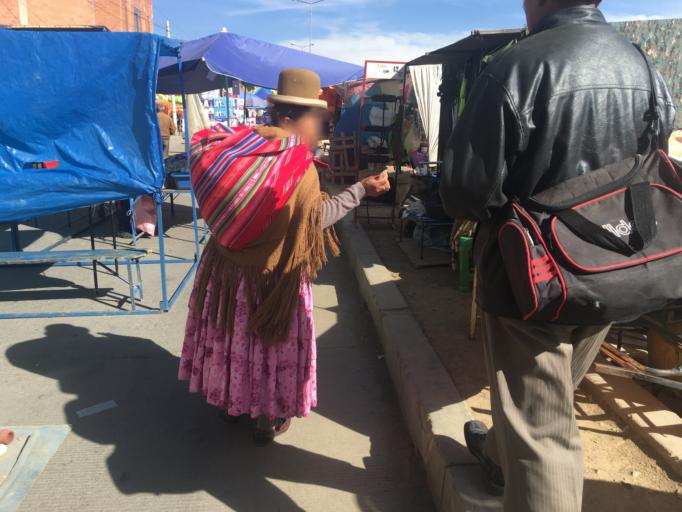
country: BO
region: La Paz
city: La Paz
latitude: -16.4942
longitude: -68.1686
